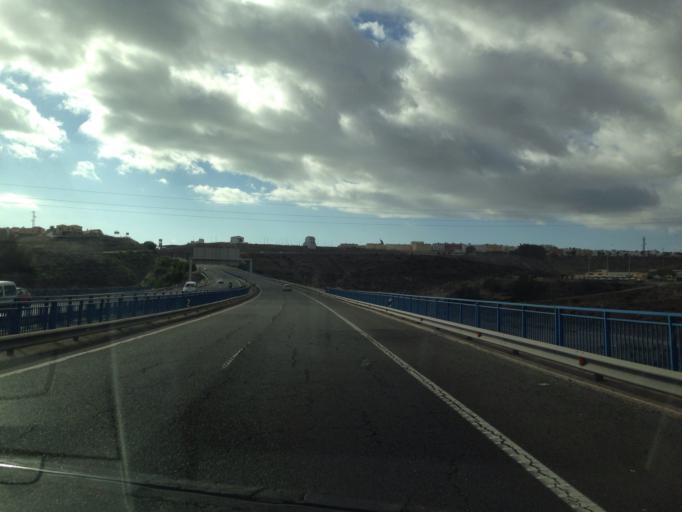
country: ES
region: Canary Islands
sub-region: Provincia de Las Palmas
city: Maspalomas
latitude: 27.7710
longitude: -15.5924
